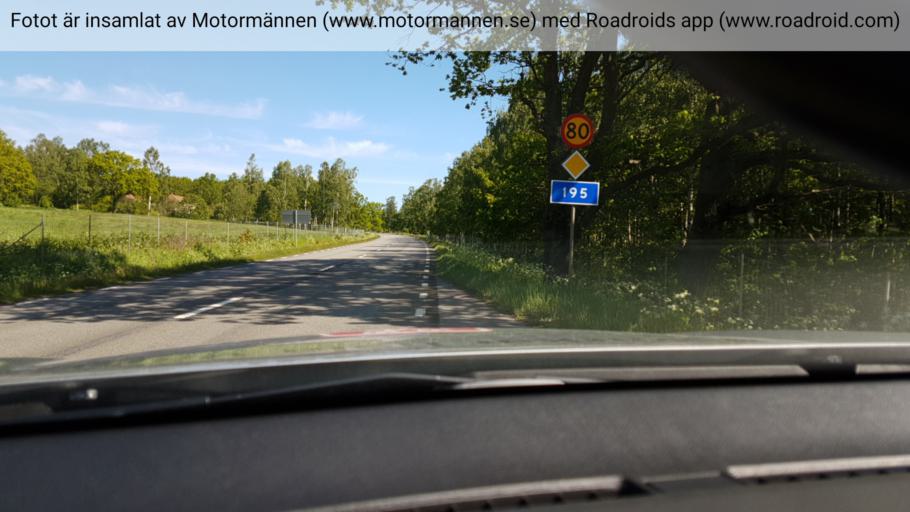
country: SE
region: Vaestra Goetaland
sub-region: Hjo Kommun
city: Hjo
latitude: 58.3515
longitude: 14.3513
